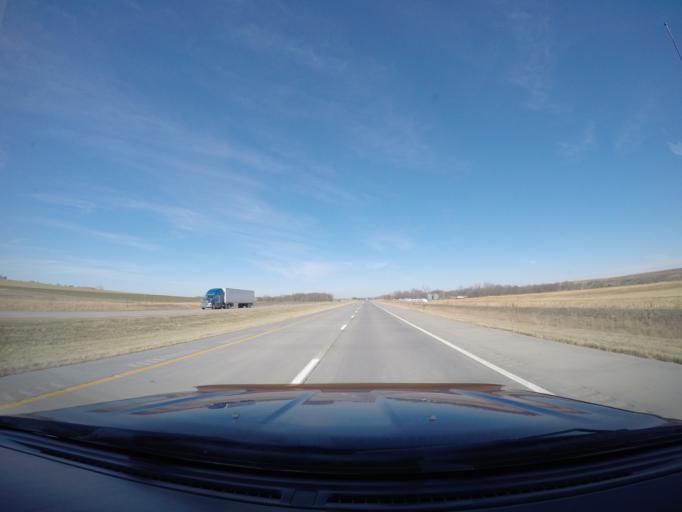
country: US
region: Kansas
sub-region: Republic County
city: Belleville
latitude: 39.7172
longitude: -97.6604
